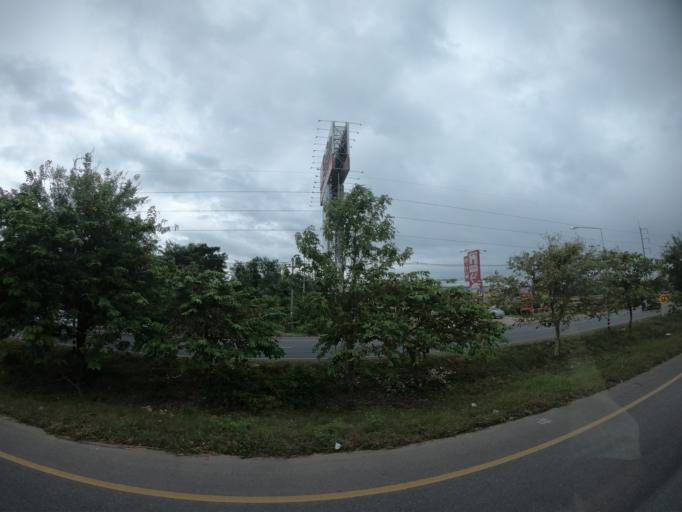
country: TH
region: Roi Et
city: Roi Et
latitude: 16.0568
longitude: 103.6198
